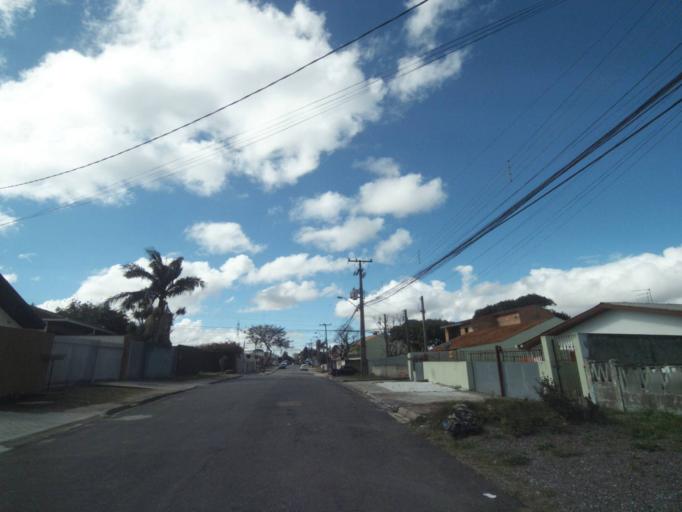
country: BR
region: Parana
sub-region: Sao Jose Dos Pinhais
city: Sao Jose dos Pinhais
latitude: -25.5318
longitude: -49.2901
